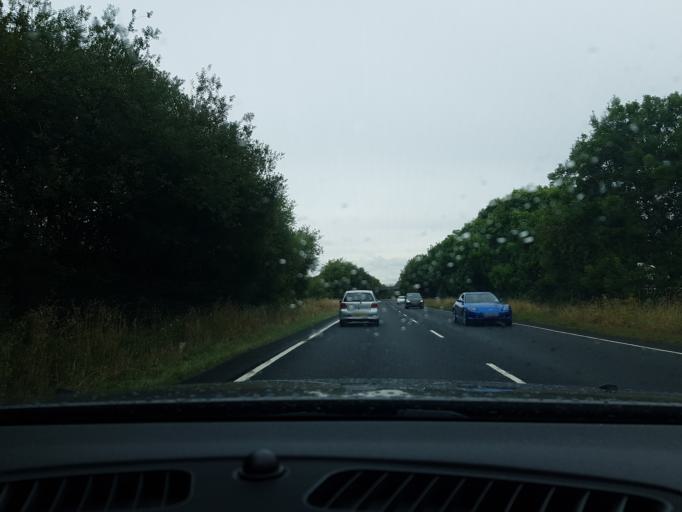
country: GB
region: England
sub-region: Hampshire
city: Odiham
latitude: 51.2630
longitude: -0.9408
